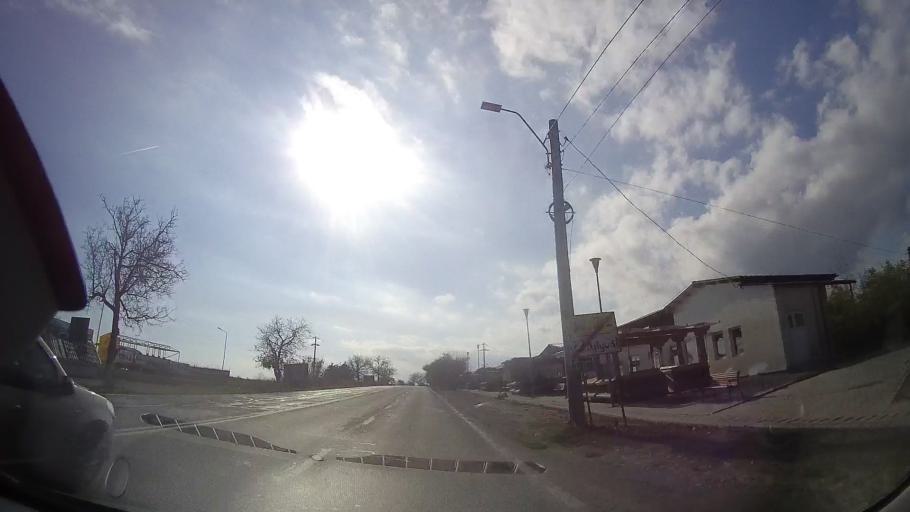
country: RO
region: Constanta
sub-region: Comuna Douazeci si Trei August
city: Douazeci si Trei August
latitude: 43.9128
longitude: 28.5788
